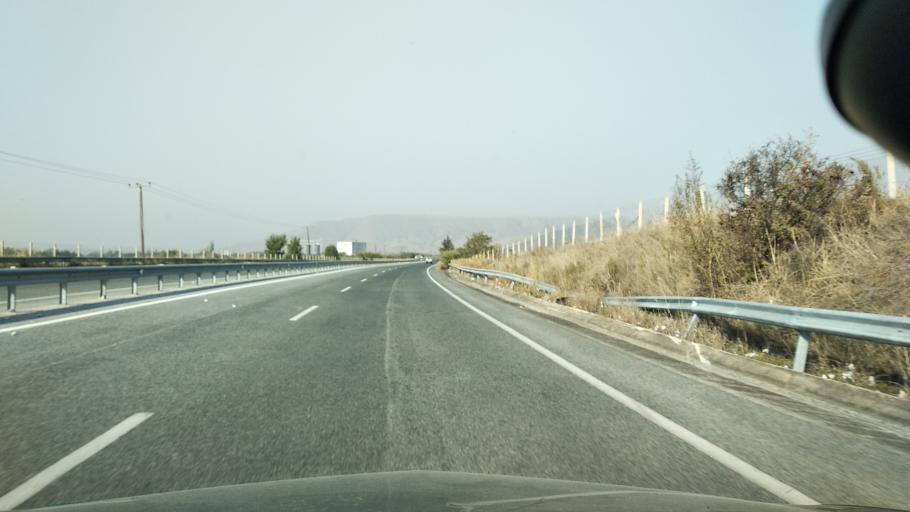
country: GR
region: Thessaly
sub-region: Trikala
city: Zarkos
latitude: 39.5882
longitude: 22.1368
